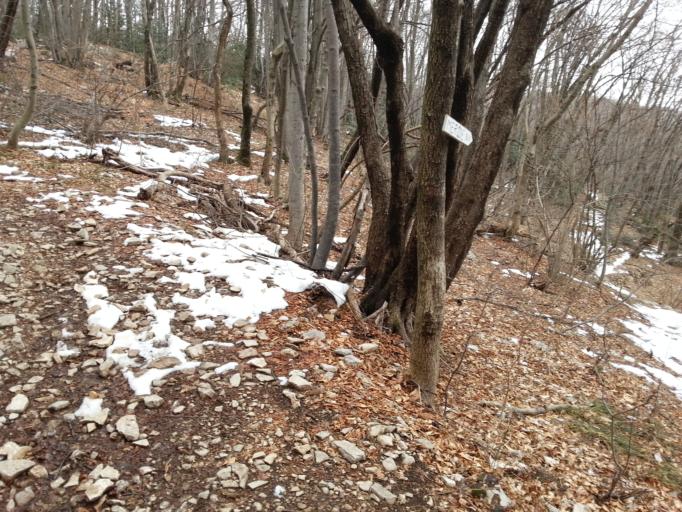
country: CH
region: Ticino
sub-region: Mendrisio District
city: Riva San Vitale
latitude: 45.9065
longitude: 8.9472
